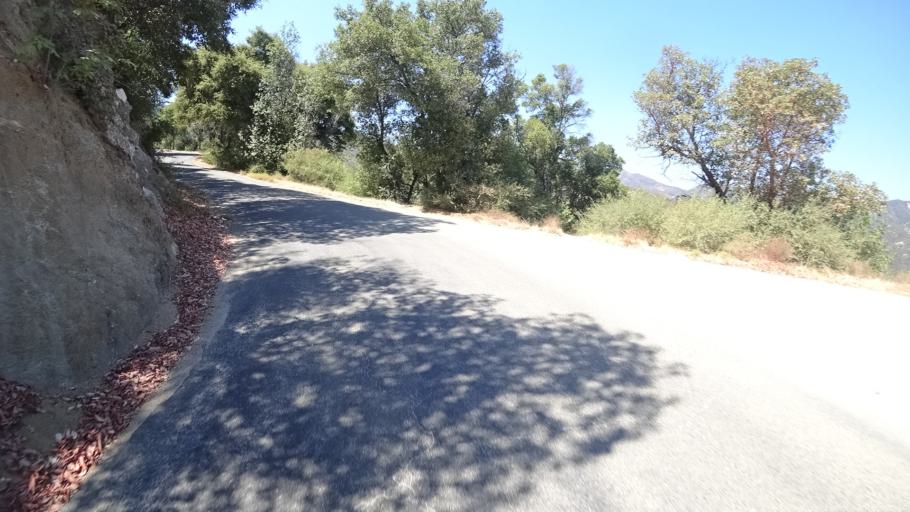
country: US
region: California
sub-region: Monterey County
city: Greenfield
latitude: 36.0139
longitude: -121.4372
